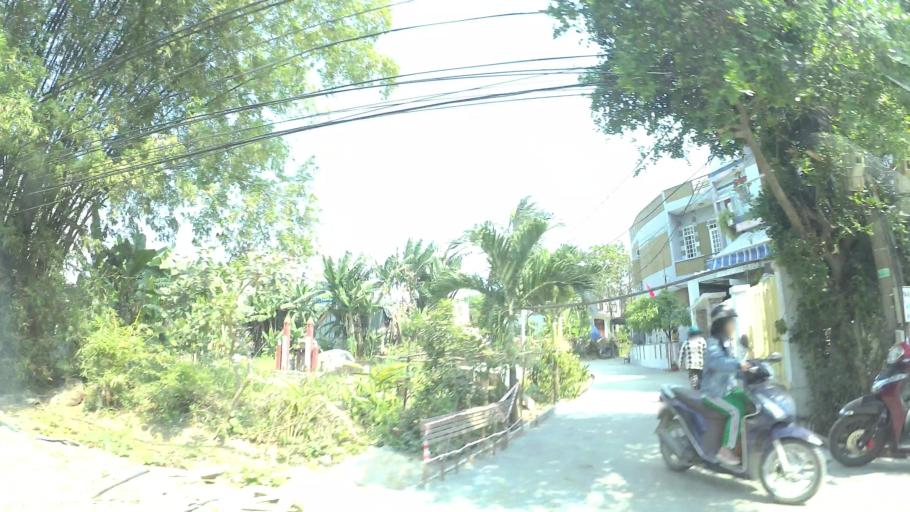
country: VN
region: Da Nang
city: Cam Le
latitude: 16.0110
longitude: 108.1983
